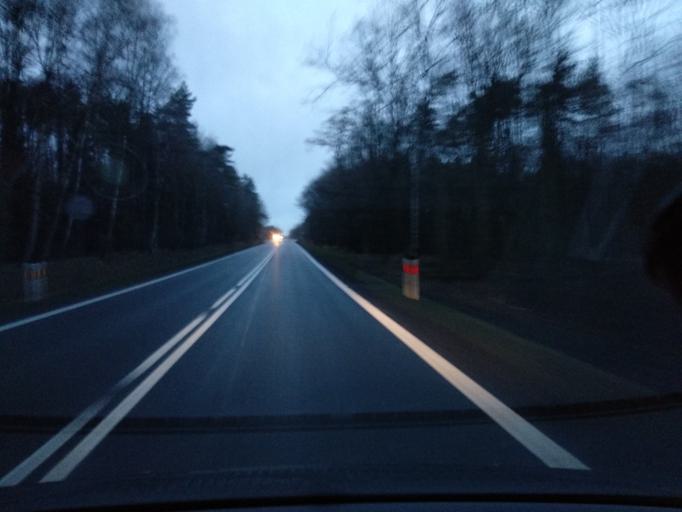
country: PL
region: Lower Silesian Voivodeship
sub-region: Powiat legnicki
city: Prochowice
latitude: 51.2490
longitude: 16.4051
